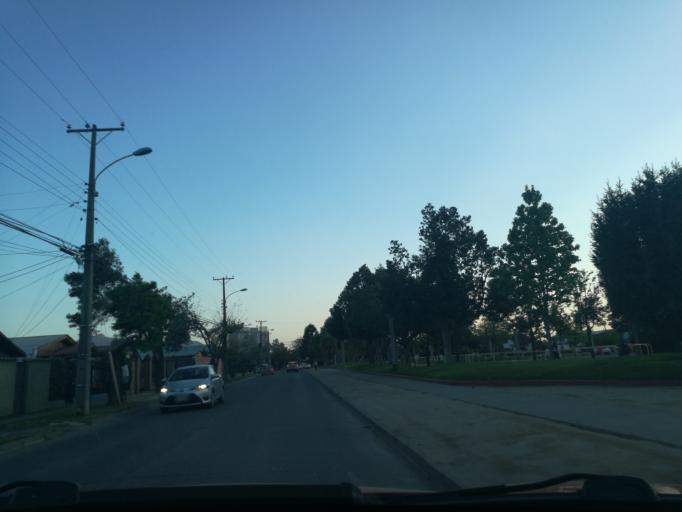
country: CL
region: O'Higgins
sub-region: Provincia de Cachapoal
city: Rancagua
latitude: -34.1594
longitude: -70.7358
